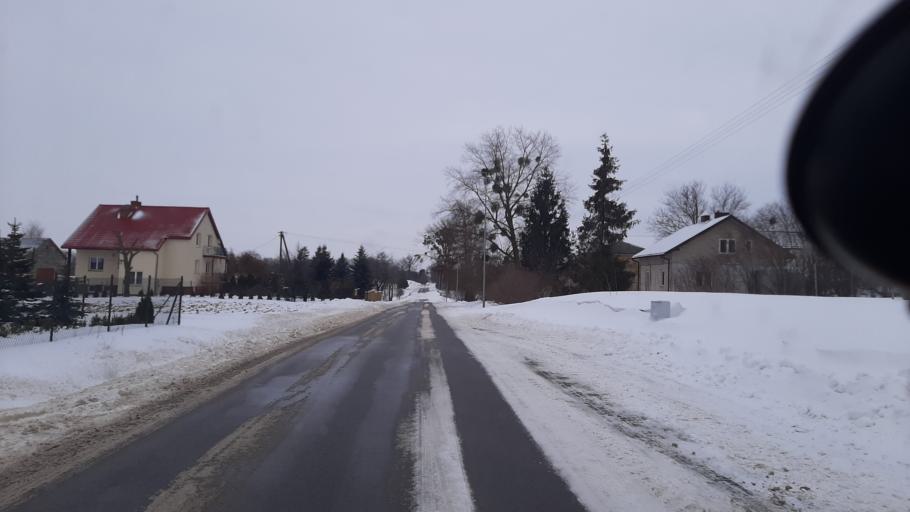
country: PL
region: Lublin Voivodeship
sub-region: Powiat lubelski
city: Garbow
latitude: 51.3255
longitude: 22.3258
